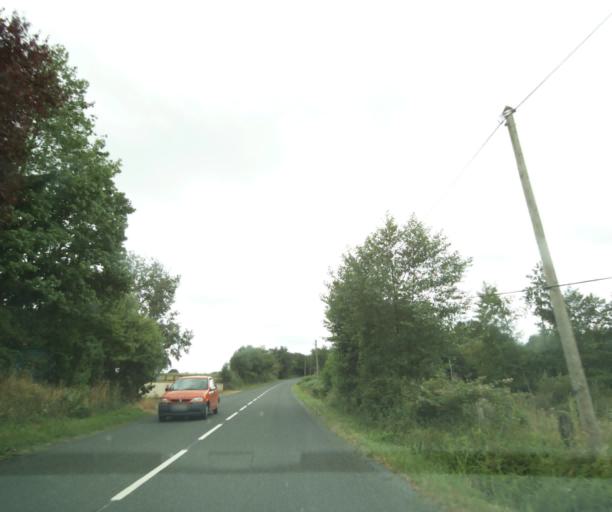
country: FR
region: Pays de la Loire
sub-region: Departement de Maine-et-Loire
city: Durtal
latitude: 47.7236
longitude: -0.2624
